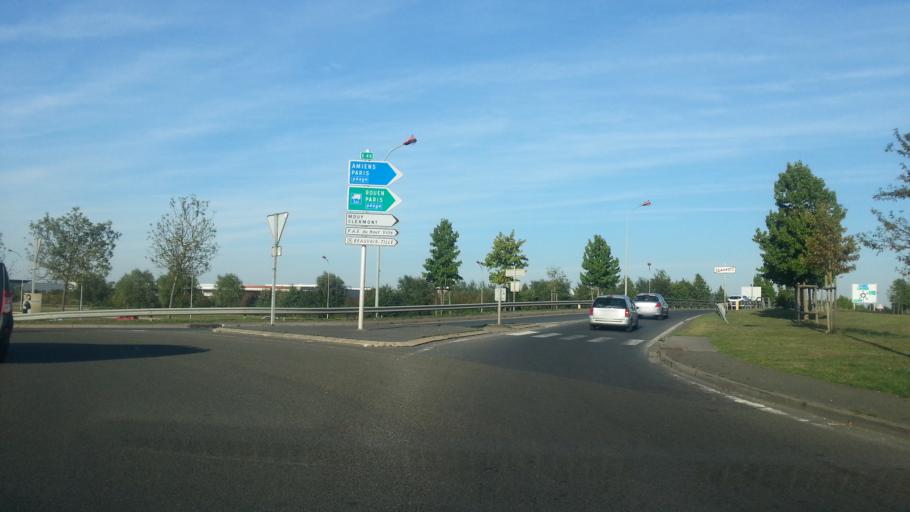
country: FR
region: Picardie
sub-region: Departement de l'Oise
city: Allonne
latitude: 49.4323
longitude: 2.1170
